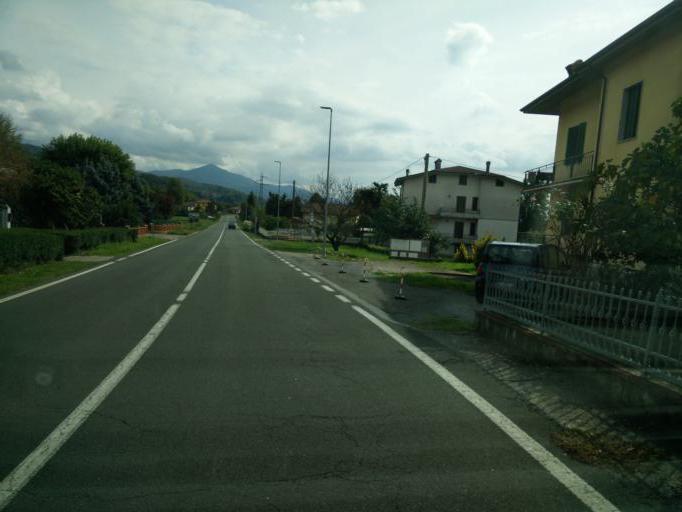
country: IT
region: Tuscany
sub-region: Provincia di Massa-Carrara
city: Filattiera
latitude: 44.3372
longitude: 9.9162
